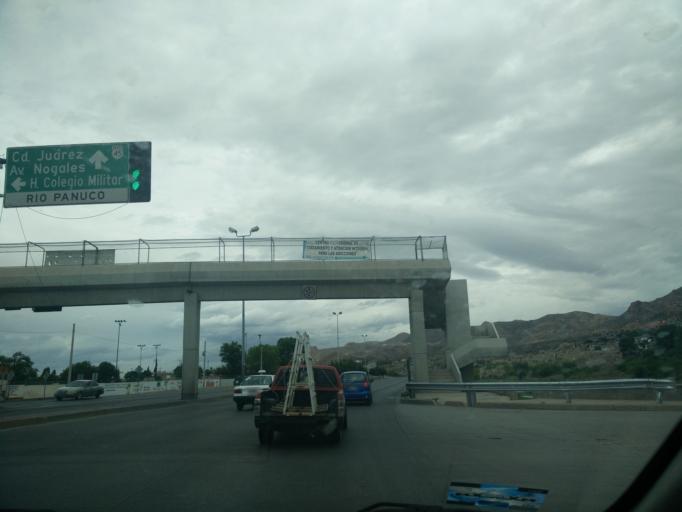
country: MX
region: Chihuahua
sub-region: Chihuahua
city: Chihuahua
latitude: 28.6632
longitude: -106.0686
